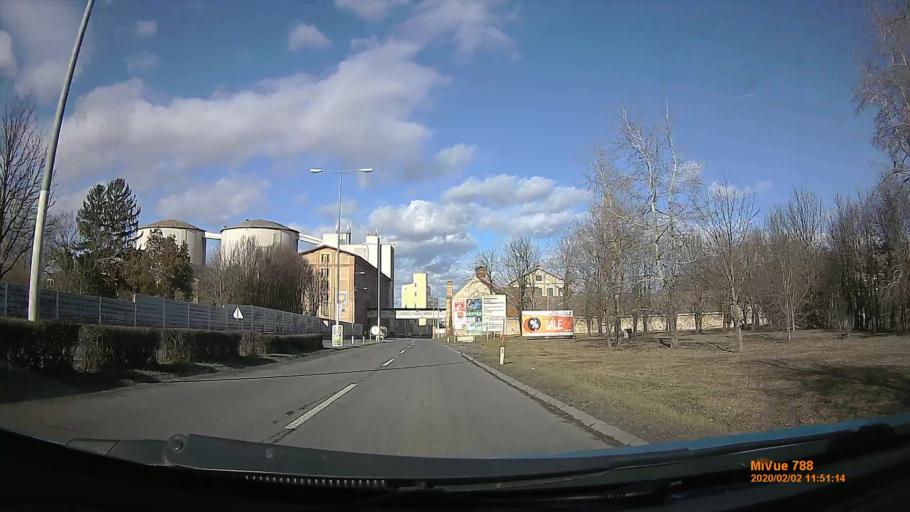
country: AT
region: Burgenland
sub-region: Eisenstadt-Umgebung
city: Zagersdorf
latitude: 47.7681
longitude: 16.5318
